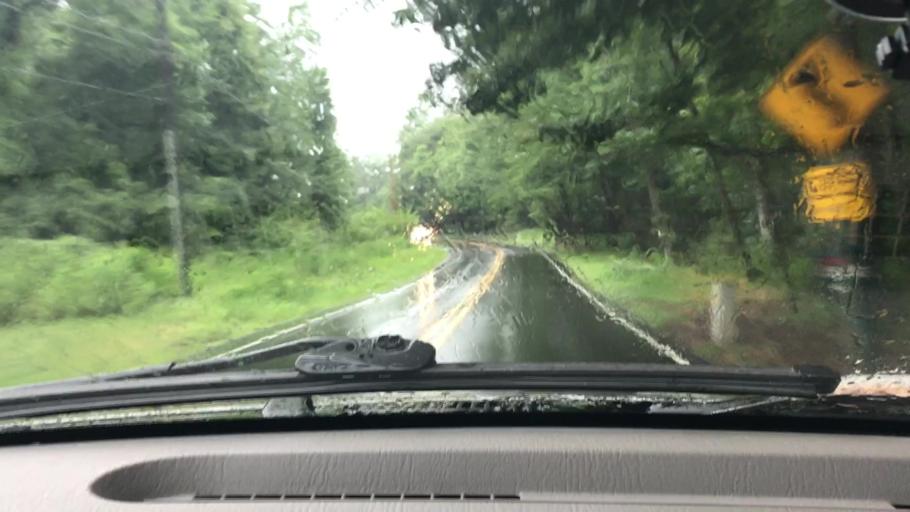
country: US
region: Pennsylvania
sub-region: Lancaster County
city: Elizabethtown
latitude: 40.1446
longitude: -76.6431
